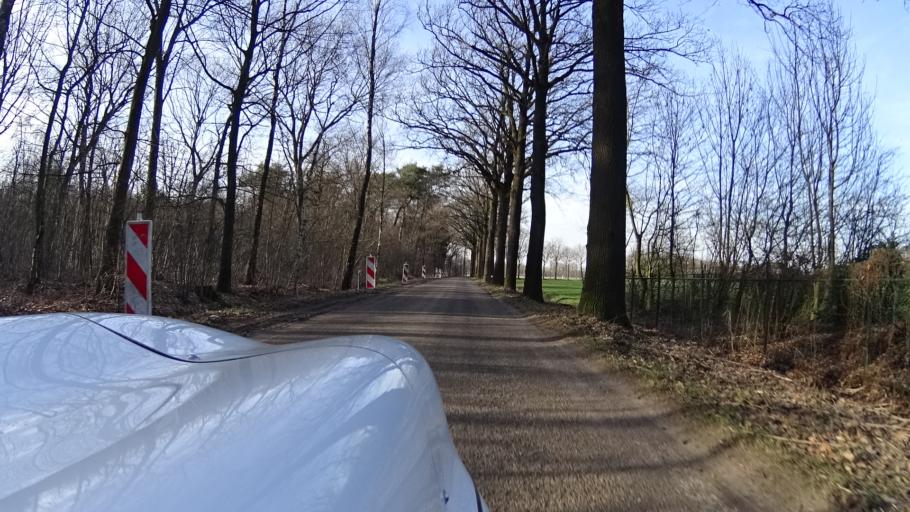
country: NL
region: North Brabant
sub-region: Gemeente Veghel
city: Erp
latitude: 51.5737
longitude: 5.6273
